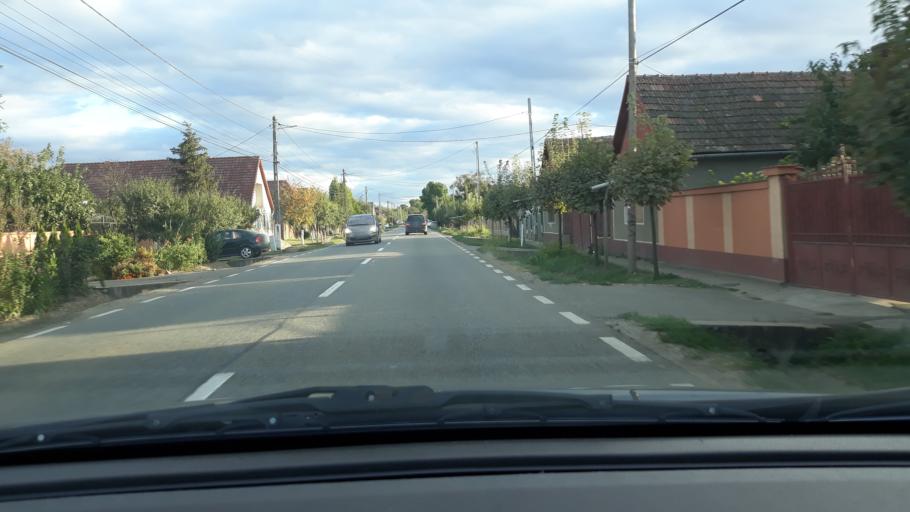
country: RO
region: Bihor
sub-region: Comuna Biharea
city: Biharea
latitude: 47.1640
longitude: 21.9221
